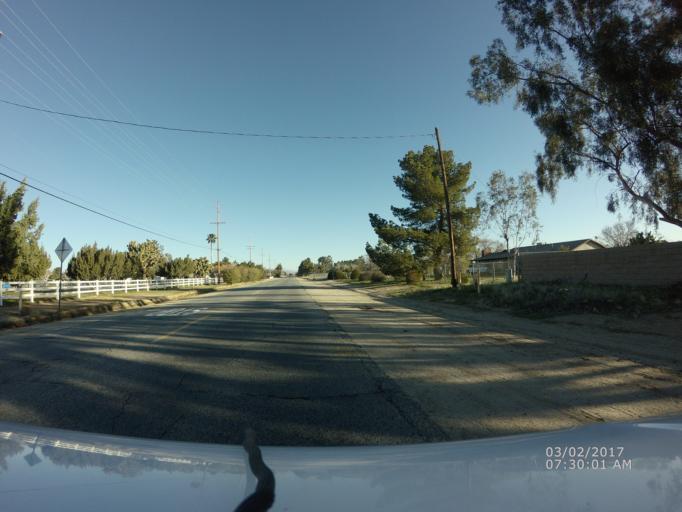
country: US
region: California
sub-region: Los Angeles County
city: Desert View Highlands
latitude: 34.6182
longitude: -118.1655
